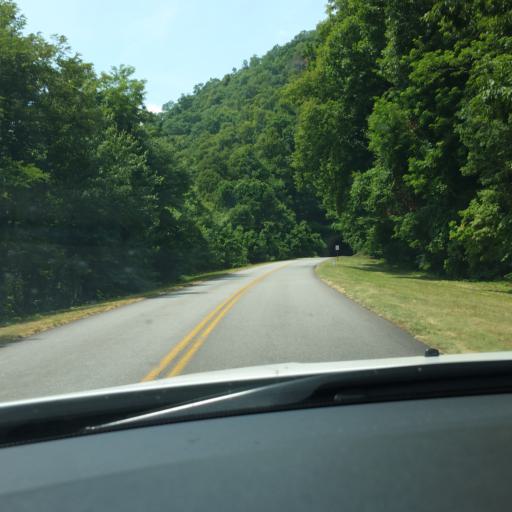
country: US
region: North Carolina
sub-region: Buncombe County
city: Avery Creek
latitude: 35.4518
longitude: -82.6408
